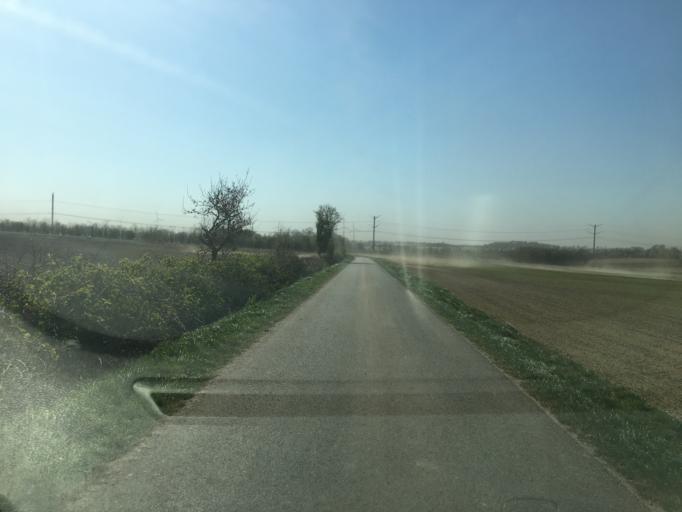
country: DK
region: South Denmark
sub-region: Aabenraa Kommune
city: Rodekro
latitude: 55.1067
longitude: 9.2270
